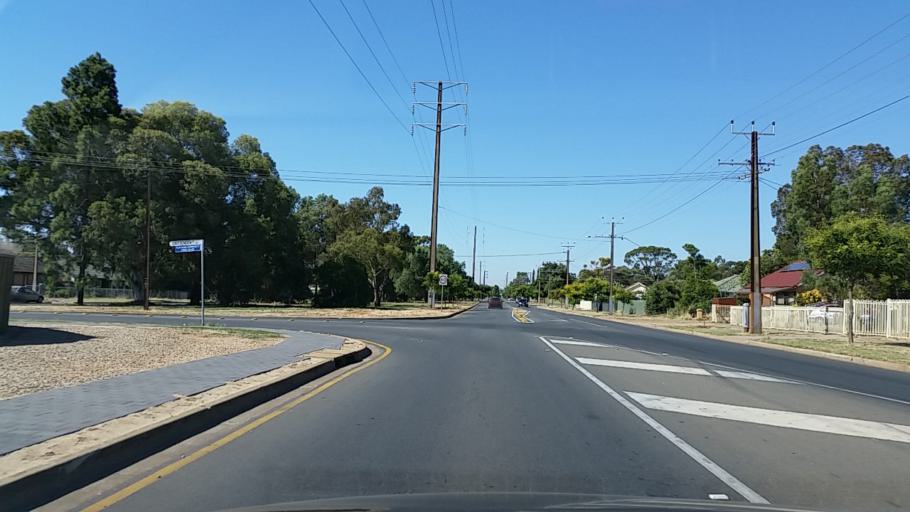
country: AU
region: South Australia
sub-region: Playford
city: Smithfield
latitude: -34.6783
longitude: 138.6822
